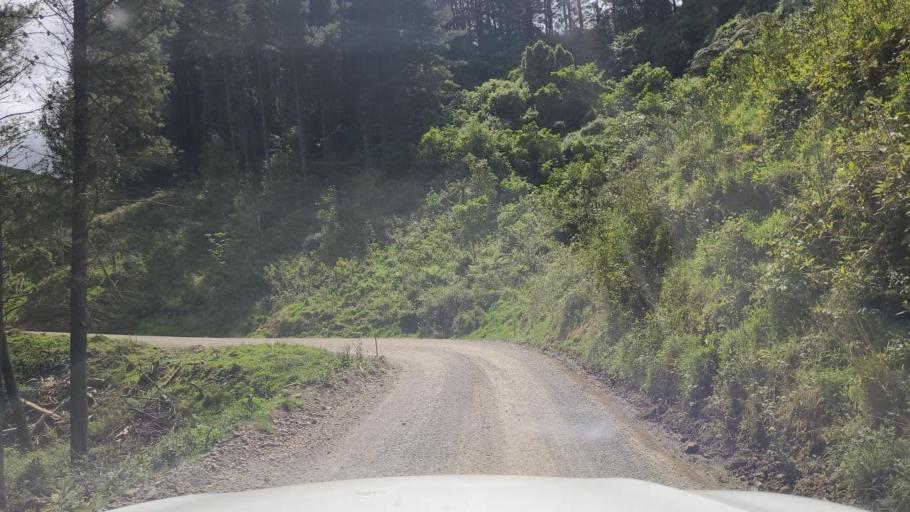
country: NZ
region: Hawke's Bay
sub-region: Napier City
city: Taradale
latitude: -39.2676
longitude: 176.6542
